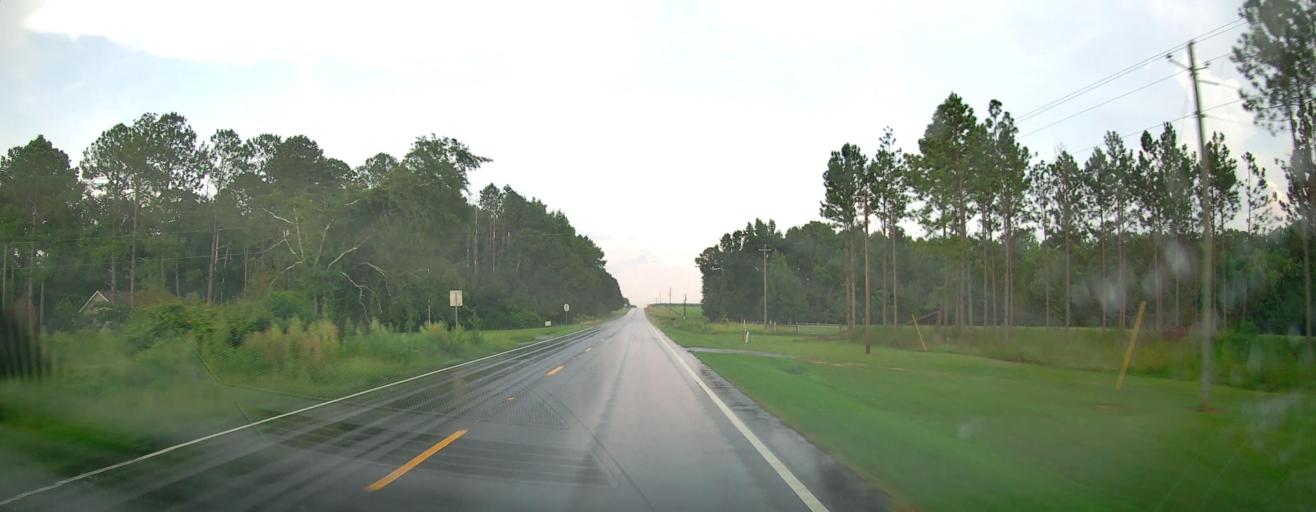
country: US
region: Georgia
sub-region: Dodge County
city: Chester
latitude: 32.5540
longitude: -83.1443
